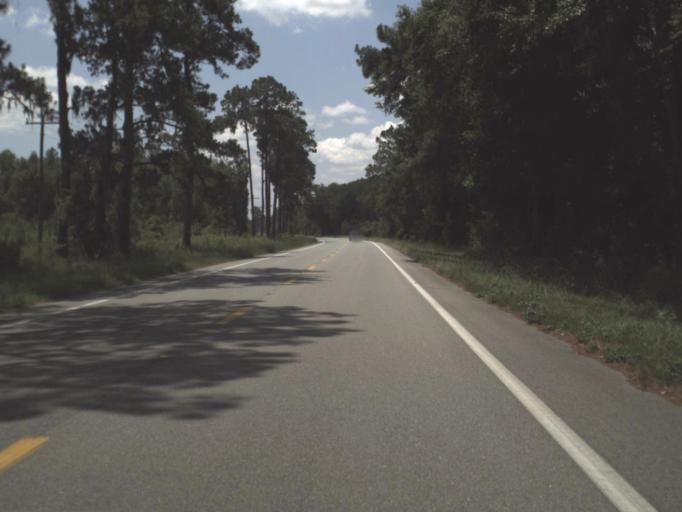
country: US
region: Florida
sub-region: Madison County
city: Madison
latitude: 30.5066
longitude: -83.6329
